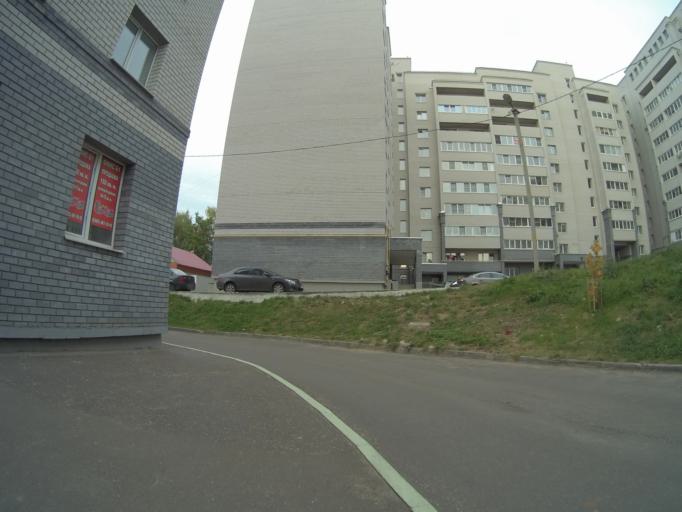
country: RU
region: Vladimir
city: Vladimir
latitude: 56.1267
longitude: 40.3559
